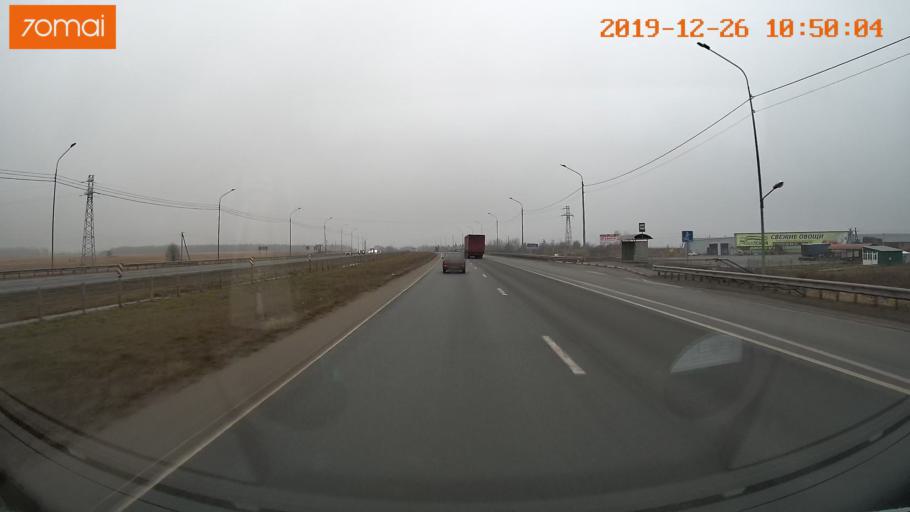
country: RU
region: Vologda
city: Molochnoye
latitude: 59.2103
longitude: 39.6982
